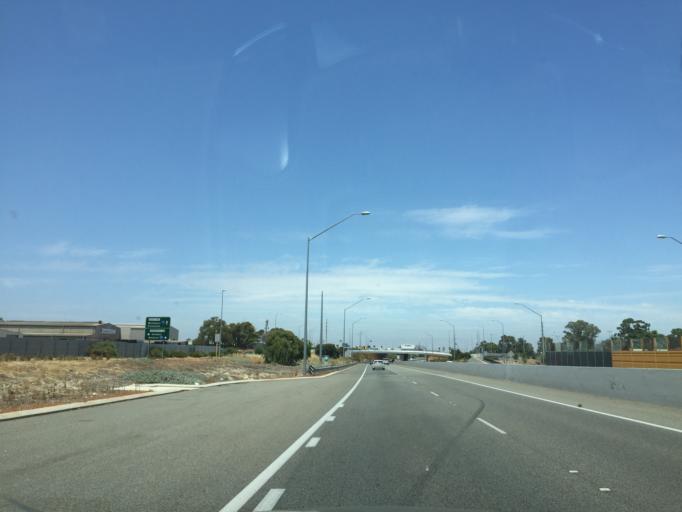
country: AU
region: Western Australia
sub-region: Belmont
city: Kewdale
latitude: -31.9707
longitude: 115.9515
